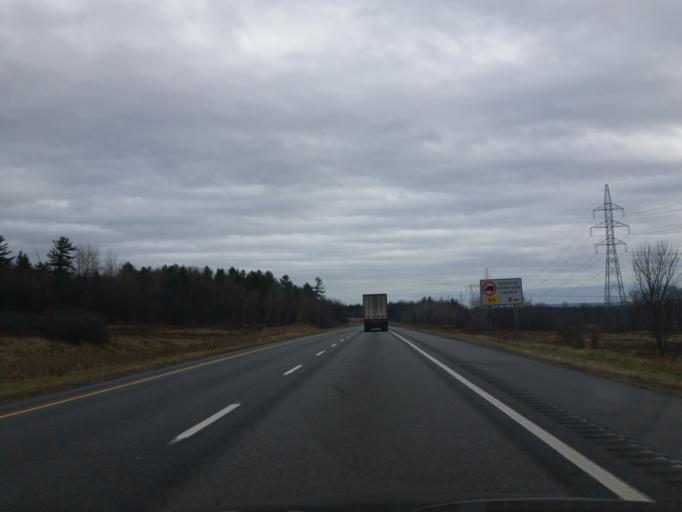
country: CA
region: Ontario
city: Clarence-Rockland
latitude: 45.5418
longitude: -75.4607
